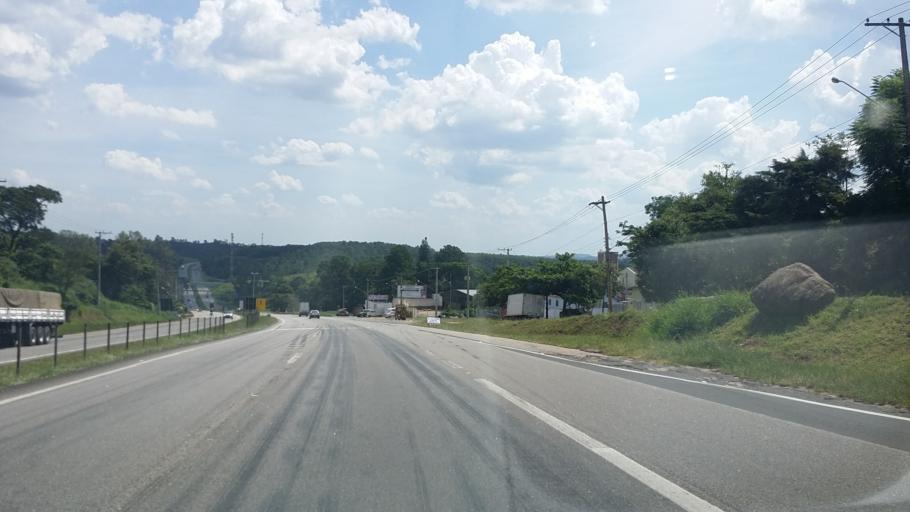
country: BR
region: Sao Paulo
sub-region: Itupeva
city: Itupeva
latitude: -23.1900
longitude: -46.9879
